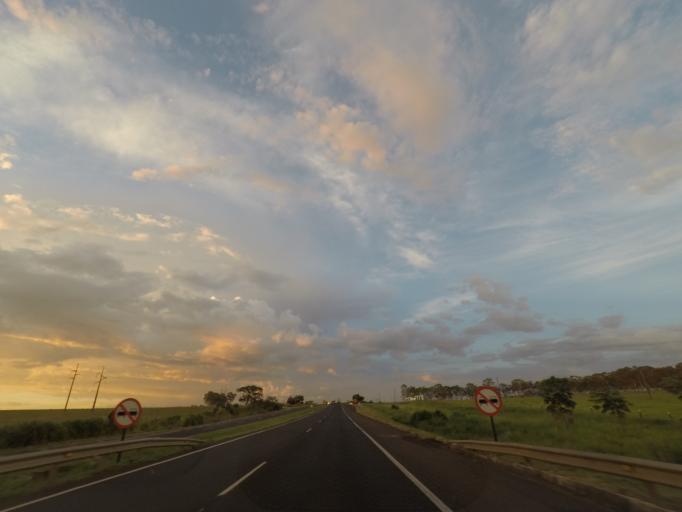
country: BR
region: Minas Gerais
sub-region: Uberaba
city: Uberaba
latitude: -19.6337
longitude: -48.0123
